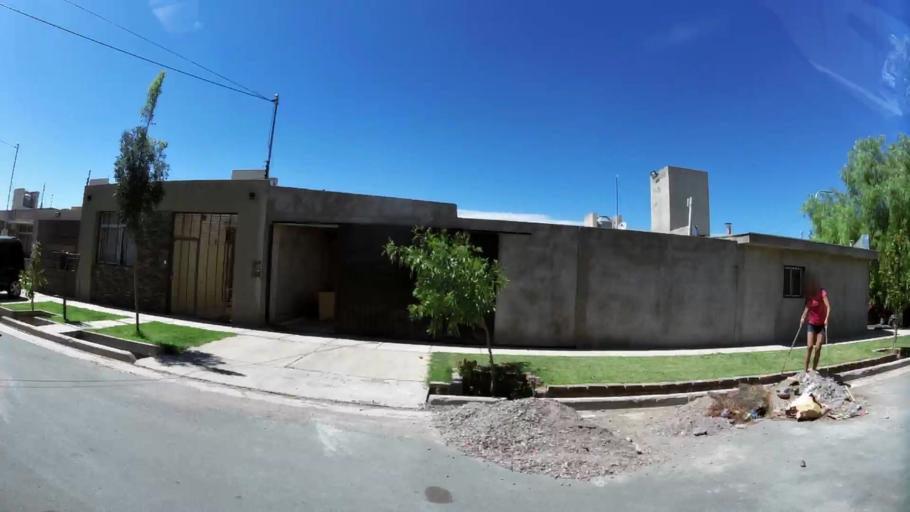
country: AR
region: Mendoza
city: Las Heras
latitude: -32.8355
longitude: -68.8689
